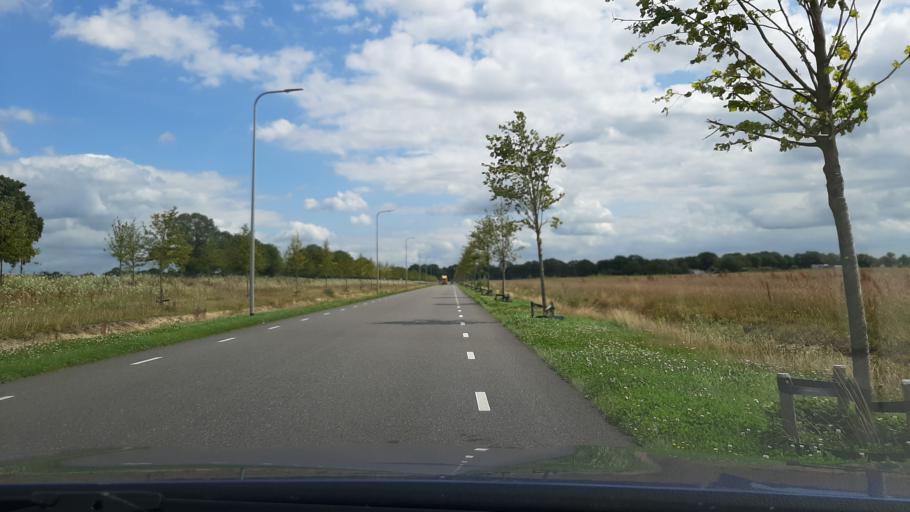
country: NL
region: Drenthe
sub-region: Gemeente Hoogeveen
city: Hoogeveen
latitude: 52.7006
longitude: 6.5236
